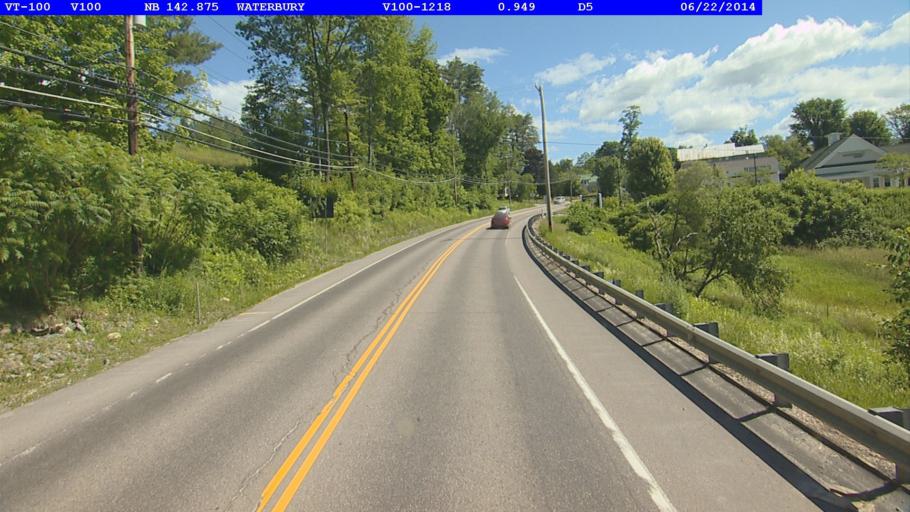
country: US
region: Vermont
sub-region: Washington County
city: Waterbury
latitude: 44.3484
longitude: -72.7448
